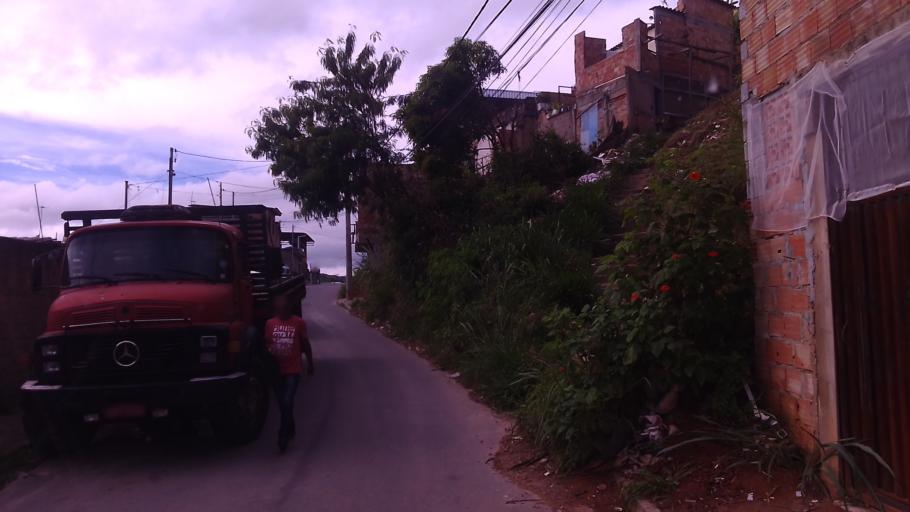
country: BR
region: Minas Gerais
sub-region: Santa Luzia
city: Santa Luzia
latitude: -19.8372
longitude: -43.8988
